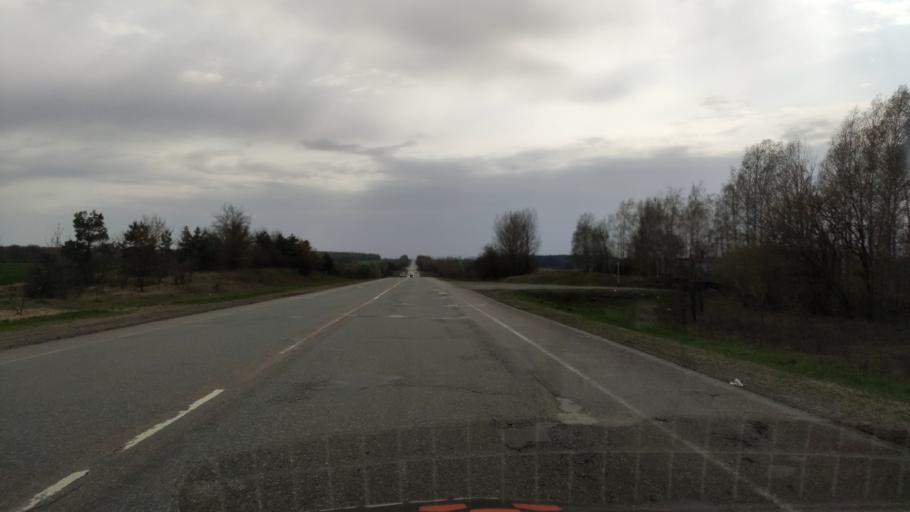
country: RU
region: Kursk
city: Gorshechnoye
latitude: 51.4477
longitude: 37.9133
